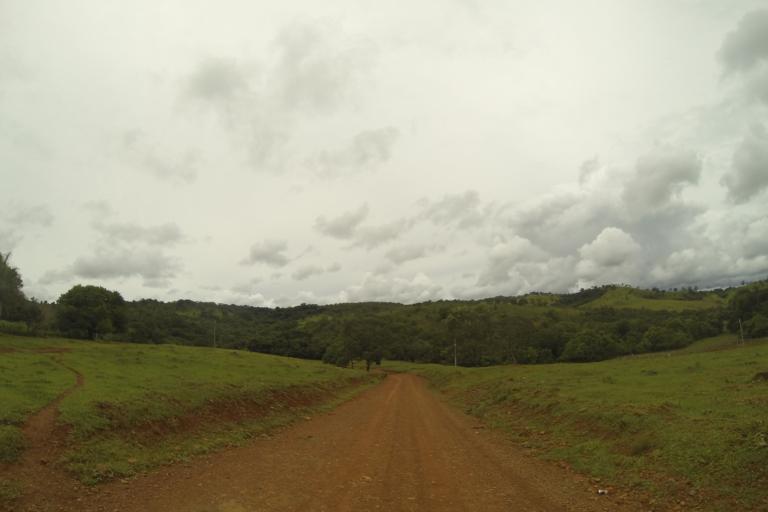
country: BR
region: Minas Gerais
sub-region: Ibia
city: Ibia
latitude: -19.6556
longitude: -46.7002
